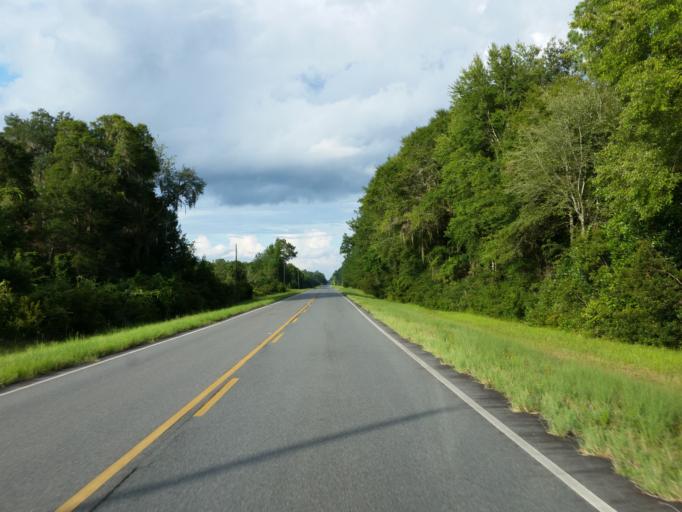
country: US
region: Florida
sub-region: Hamilton County
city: Jasper
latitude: 30.6157
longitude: -82.6312
